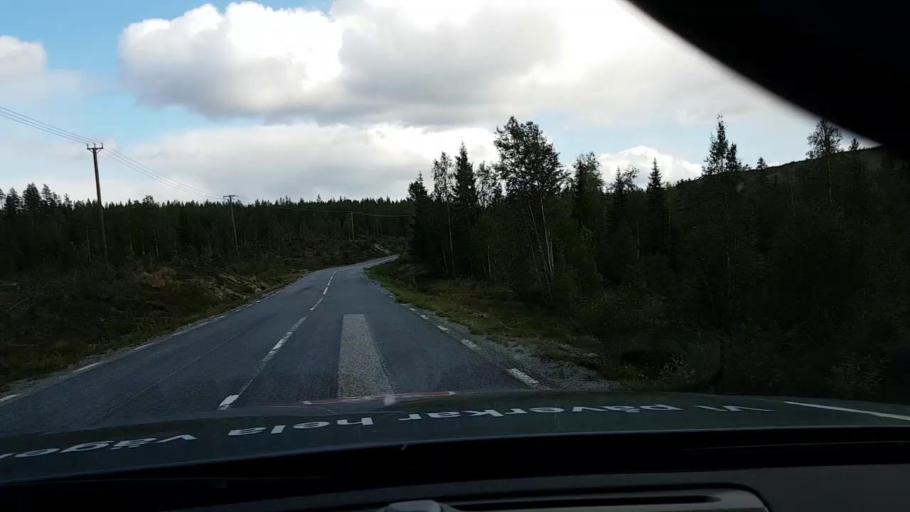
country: SE
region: Vaesterbotten
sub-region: Asele Kommun
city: Asele
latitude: 63.8010
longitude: 17.5538
